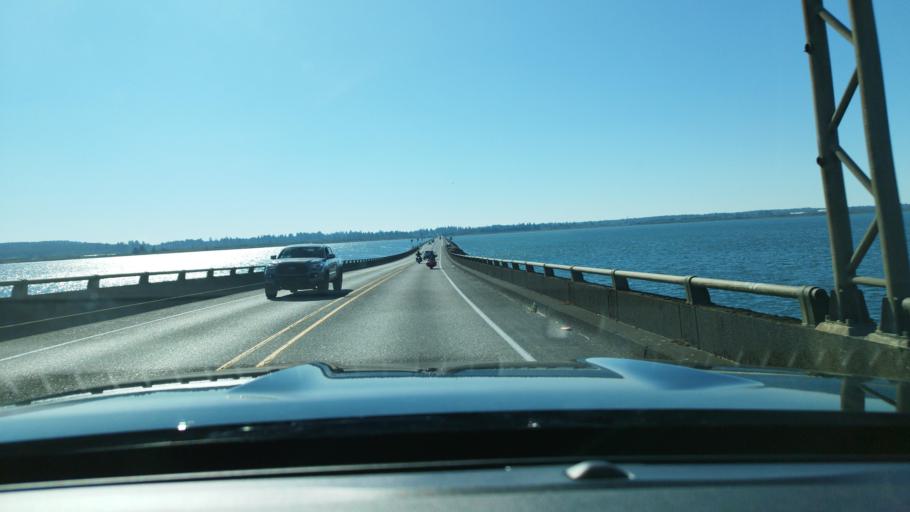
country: US
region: Oregon
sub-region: Clatsop County
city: Astoria
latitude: 46.1769
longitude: -123.8646
